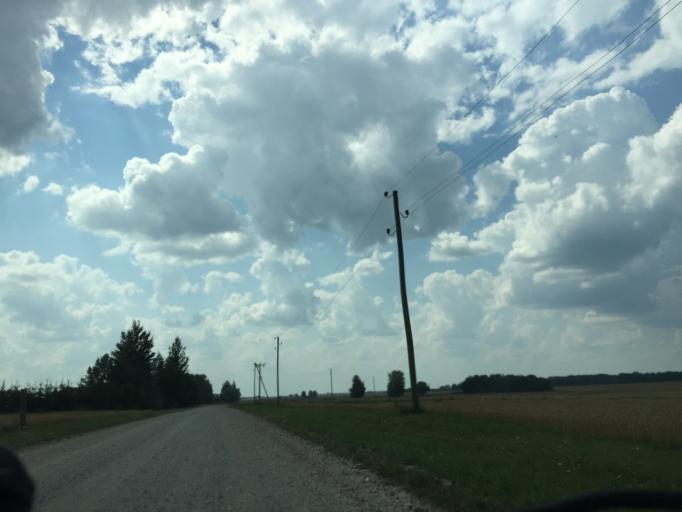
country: LT
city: Zagare
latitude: 56.3409
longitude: 23.1262
